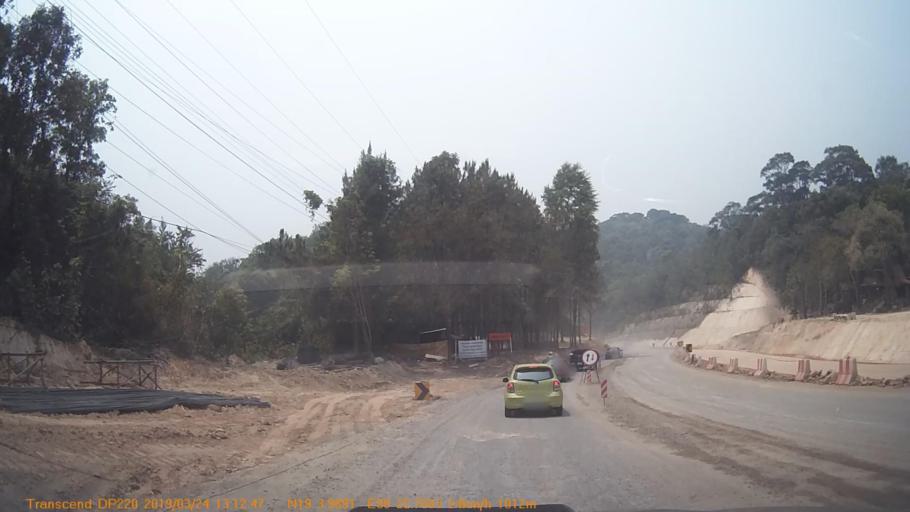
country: TH
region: Lampang
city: Wang Nuea
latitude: 19.0664
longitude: 99.3785
